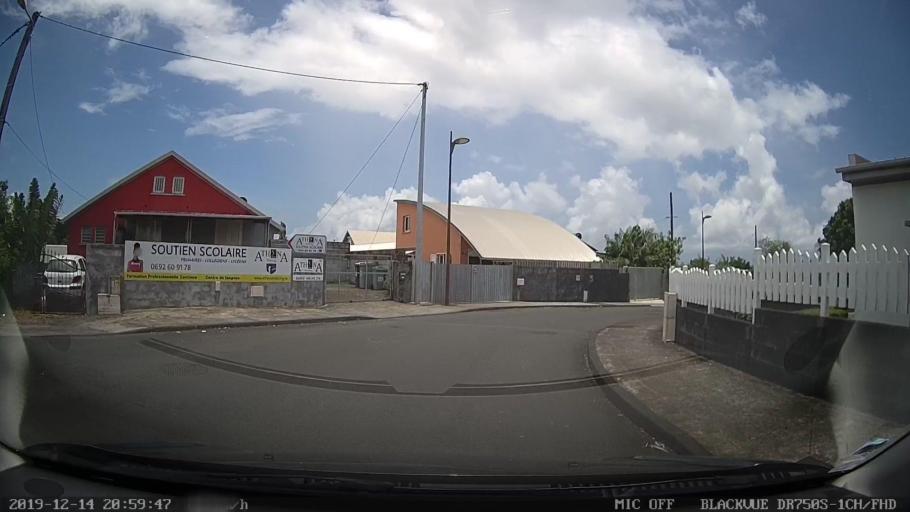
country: RE
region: Reunion
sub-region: Reunion
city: Saint-Andre
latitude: -20.9700
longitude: 55.6571
